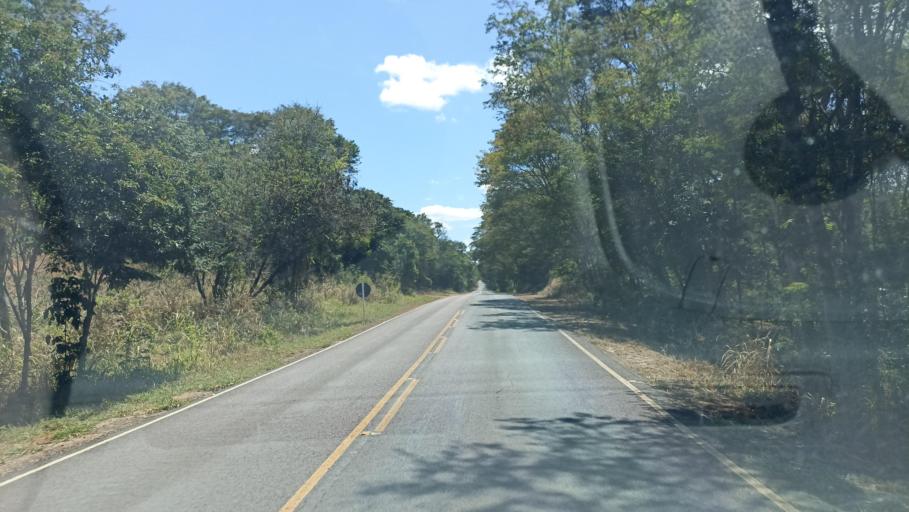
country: BR
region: Bahia
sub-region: Andarai
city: Vera Cruz
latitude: -12.7831
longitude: -41.3288
